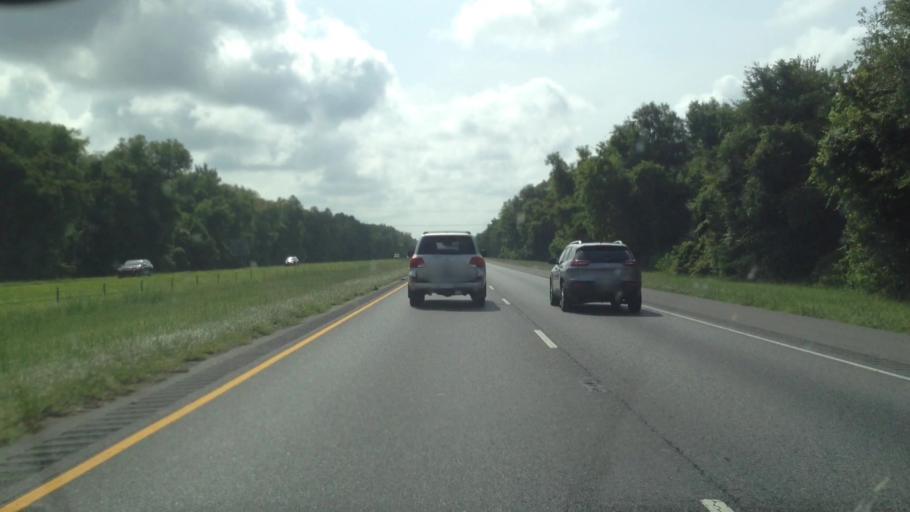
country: US
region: Louisiana
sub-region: Ascension Parish
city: Sorrento
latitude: 30.1653
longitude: -90.8546
